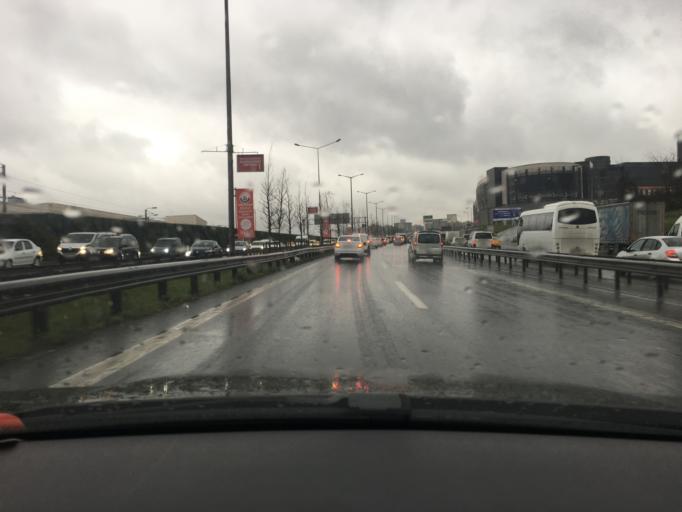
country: TR
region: Istanbul
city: Esenler
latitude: 41.0387
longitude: 28.8880
